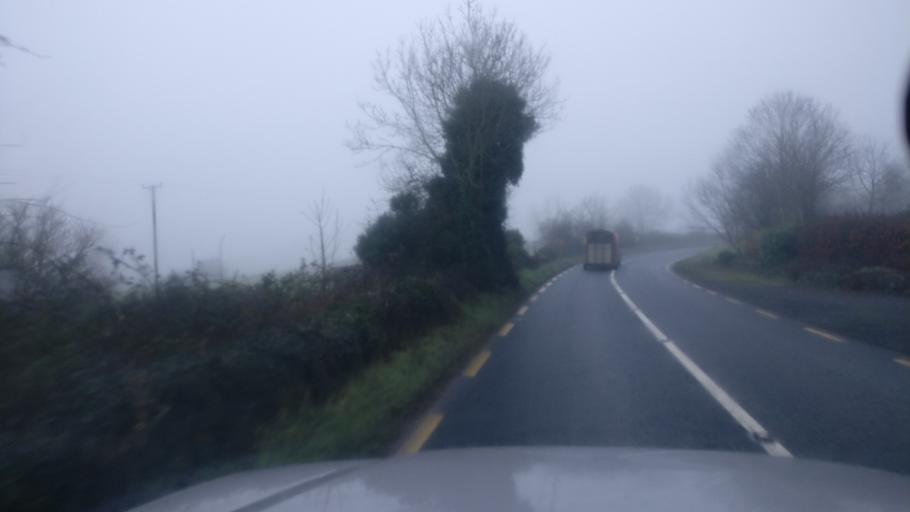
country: IE
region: Connaught
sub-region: County Galway
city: Loughrea
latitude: 53.1591
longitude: -8.6861
